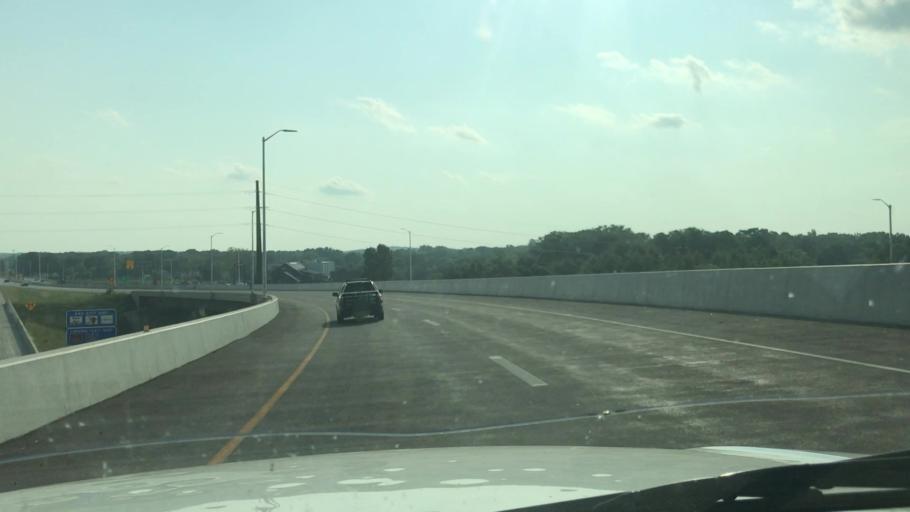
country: US
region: Wisconsin
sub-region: Brown County
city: Howard
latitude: 44.5598
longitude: -88.0519
